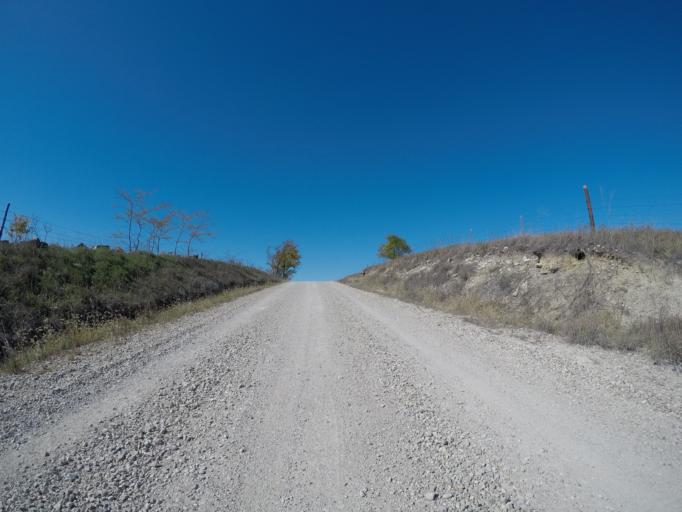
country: US
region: Kansas
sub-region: Wabaunsee County
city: Alma
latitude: 38.9758
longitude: -96.3654
